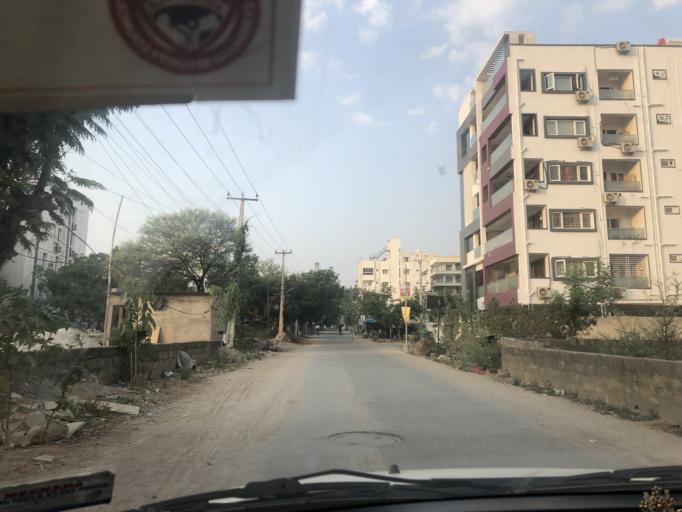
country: IN
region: Telangana
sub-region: Rangareddi
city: Kukatpalli
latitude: 17.4452
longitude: 78.3990
